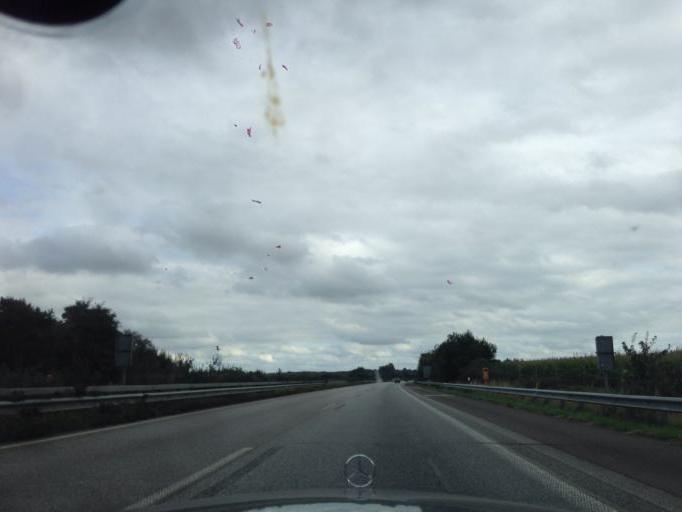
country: DE
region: Schleswig-Holstein
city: Datgen
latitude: 54.1882
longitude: 9.9319
